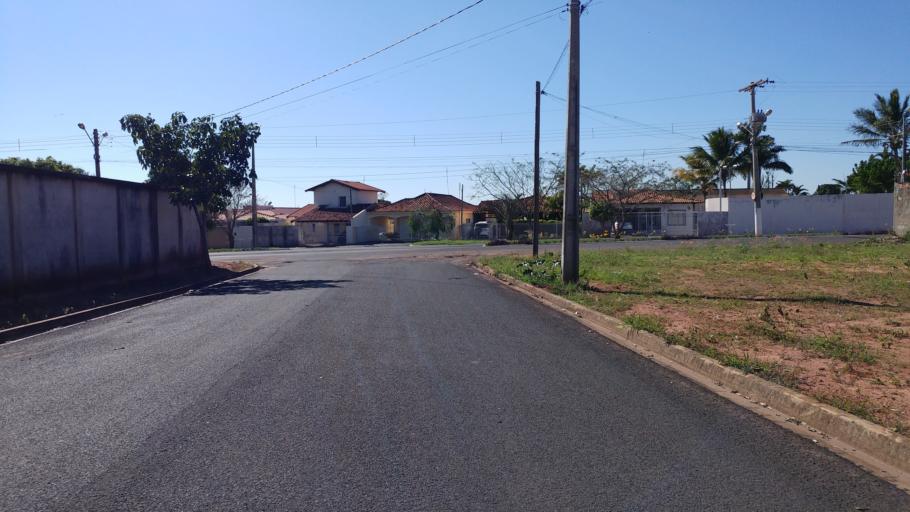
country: BR
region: Sao Paulo
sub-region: Paraguacu Paulista
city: Paraguacu Paulista
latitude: -22.4053
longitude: -50.5816
